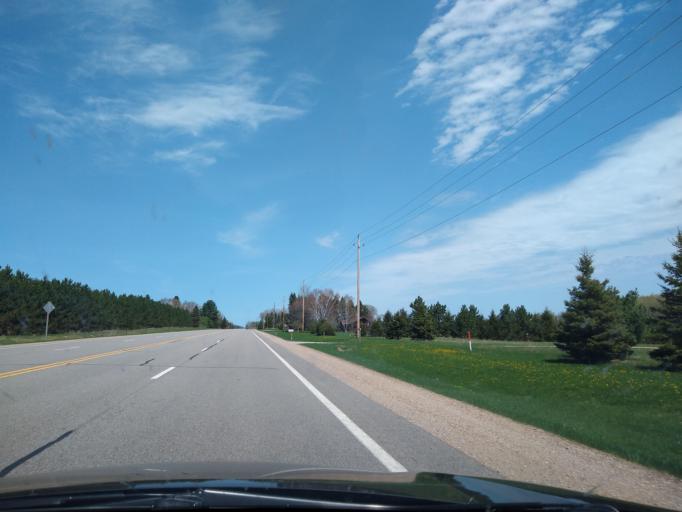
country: US
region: Michigan
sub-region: Delta County
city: Gladstone
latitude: 46.0818
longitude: -86.9808
